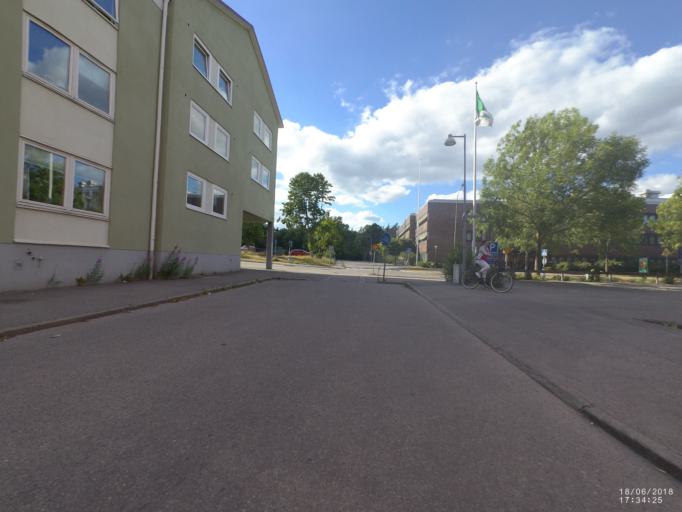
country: SE
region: Soedermanland
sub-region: Nykopings Kommun
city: Nykoping
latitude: 58.7564
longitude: 17.0147
